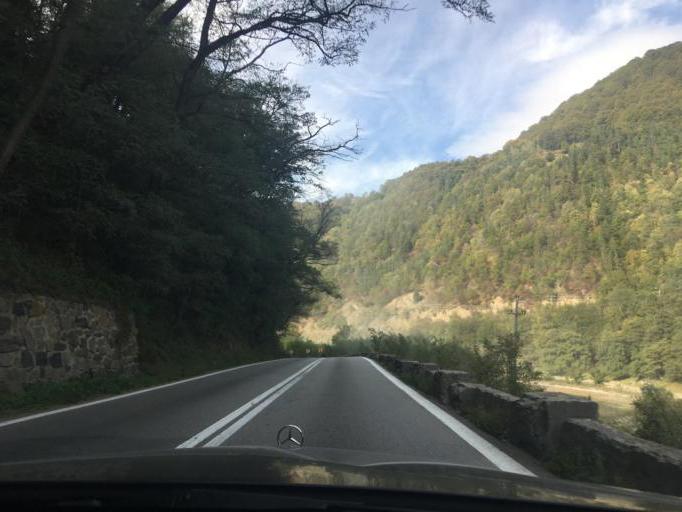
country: RO
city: Cainenii Mici
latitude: 45.5148
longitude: 24.2827
